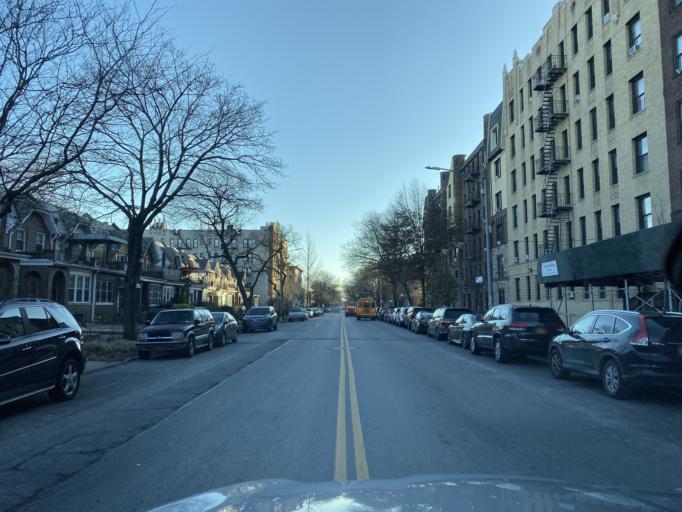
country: US
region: New York
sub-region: Kings County
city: Brooklyn
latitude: 40.6619
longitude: -73.9588
